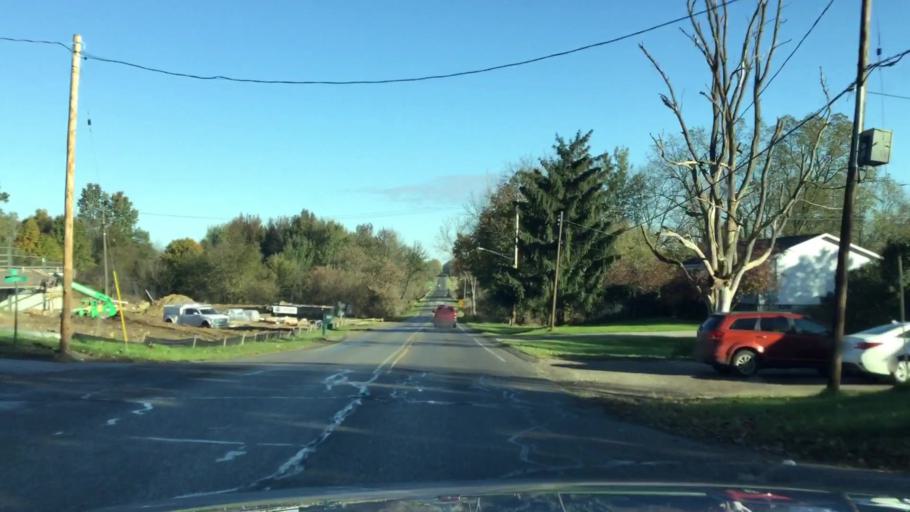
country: US
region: Michigan
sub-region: Shiawassee County
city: Durand
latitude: 42.8279
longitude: -83.9446
